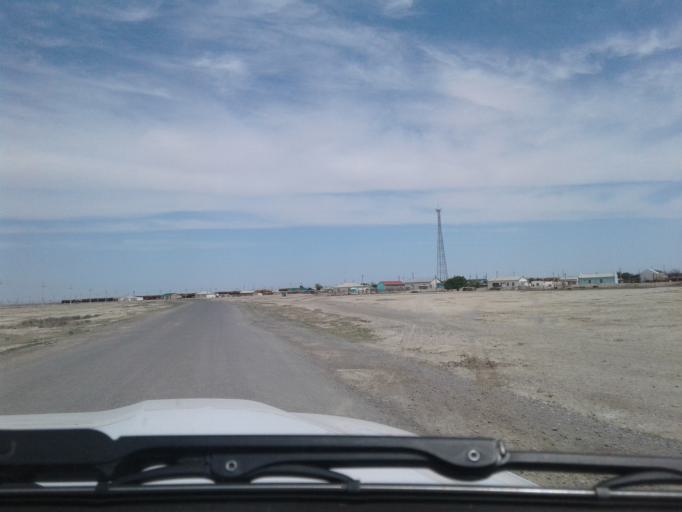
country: TM
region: Balkan
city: Gazanjyk
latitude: 39.2068
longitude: 55.7099
